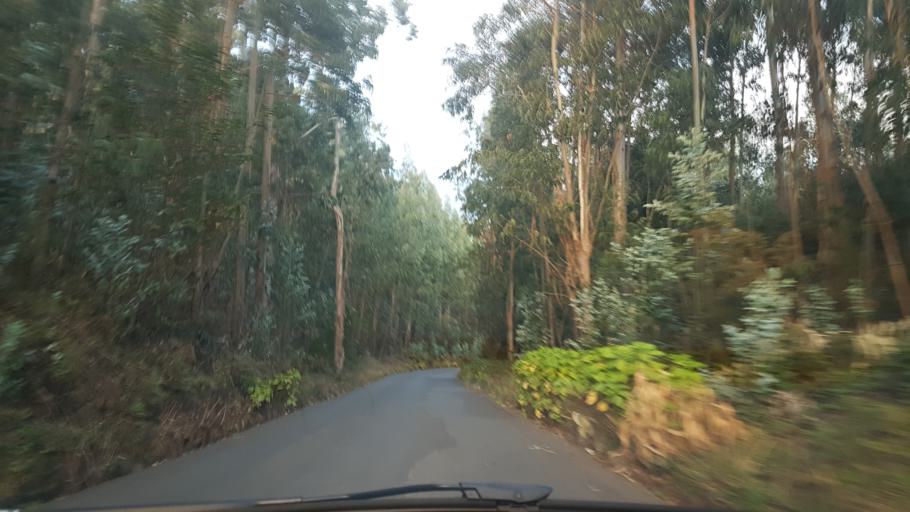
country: PT
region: Madeira
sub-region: Calheta
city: Arco da Calheta
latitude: 32.7275
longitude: -17.1090
